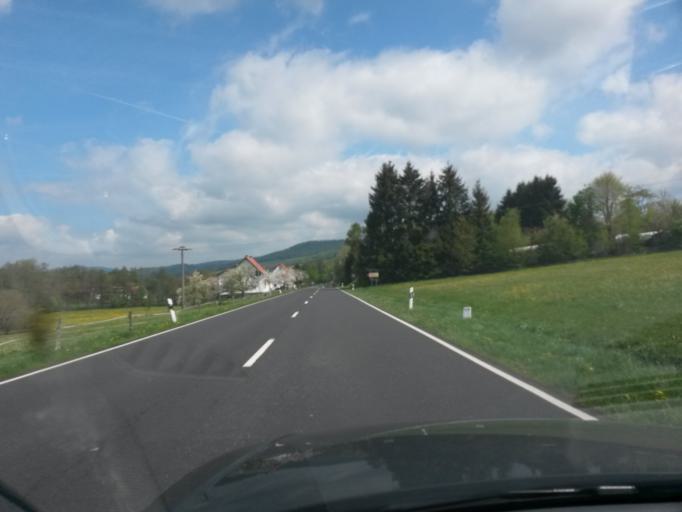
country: DE
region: Thuringia
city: Birx
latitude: 50.5097
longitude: 10.0148
